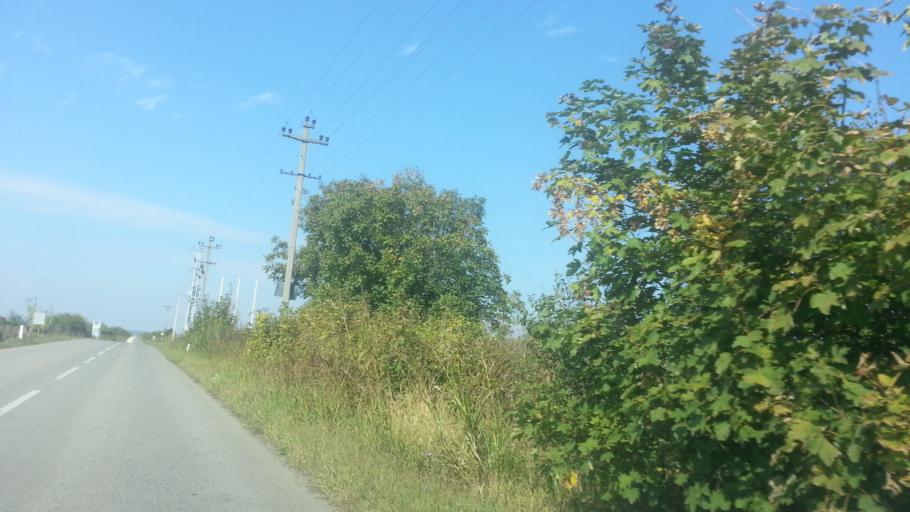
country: RS
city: Surduk
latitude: 45.0985
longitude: 20.2915
